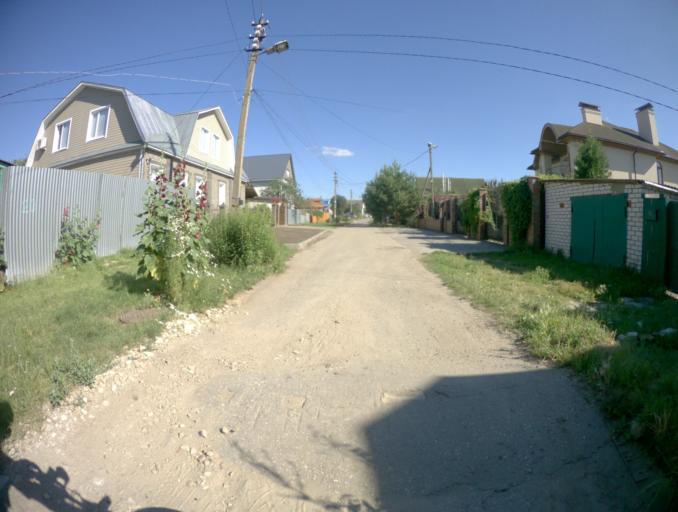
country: RU
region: Nizjnij Novgorod
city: Pavlovo
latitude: 55.9754
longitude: 43.0778
